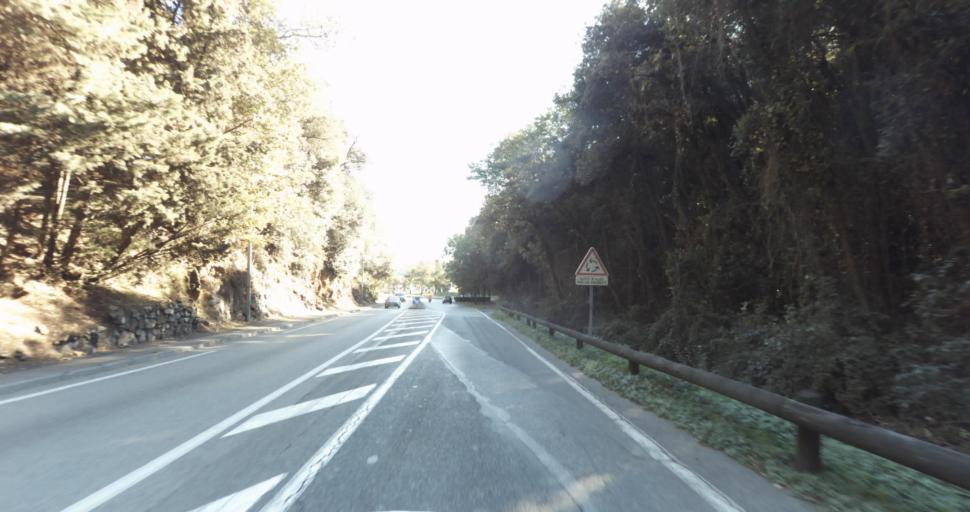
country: FR
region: Provence-Alpes-Cote d'Azur
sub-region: Departement des Alpes-Maritimes
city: Vence
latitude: 43.7160
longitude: 7.1152
